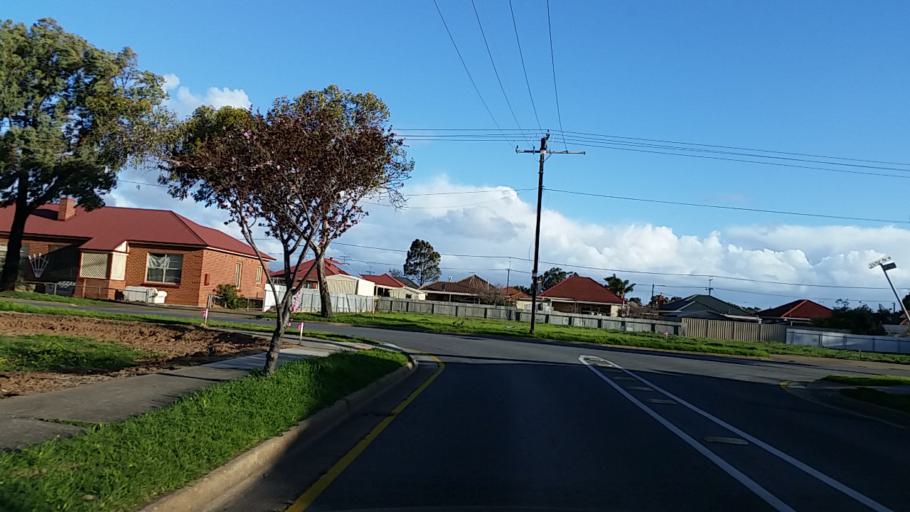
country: AU
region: South Australia
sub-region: Charles Sturt
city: Woodville West
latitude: -34.8884
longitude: 138.5297
